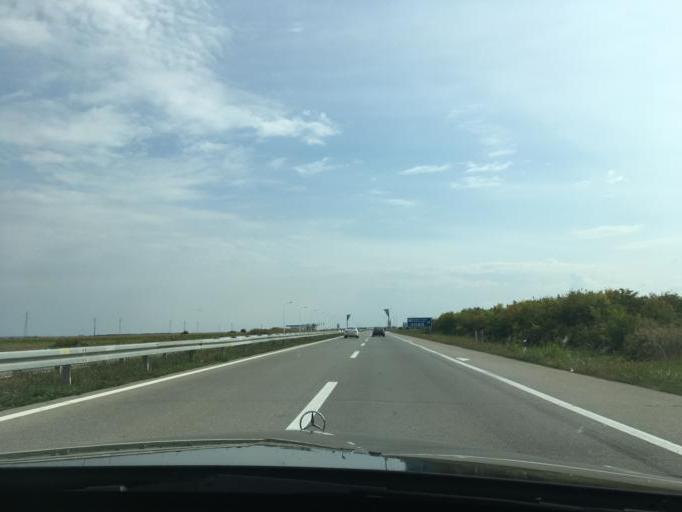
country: RS
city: Ravnje
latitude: 45.0379
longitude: 19.4437
